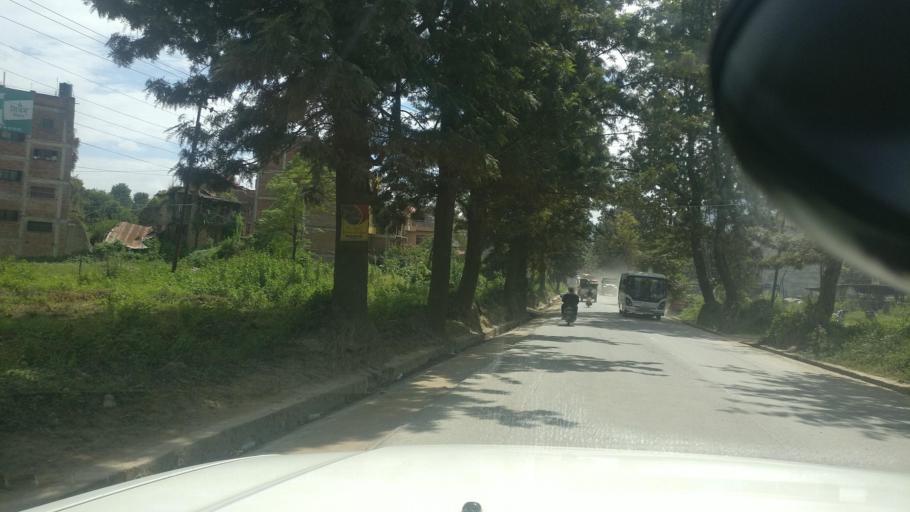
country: NP
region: Central Region
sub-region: Bagmati Zone
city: Bhaktapur
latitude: 27.6649
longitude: 85.4405
